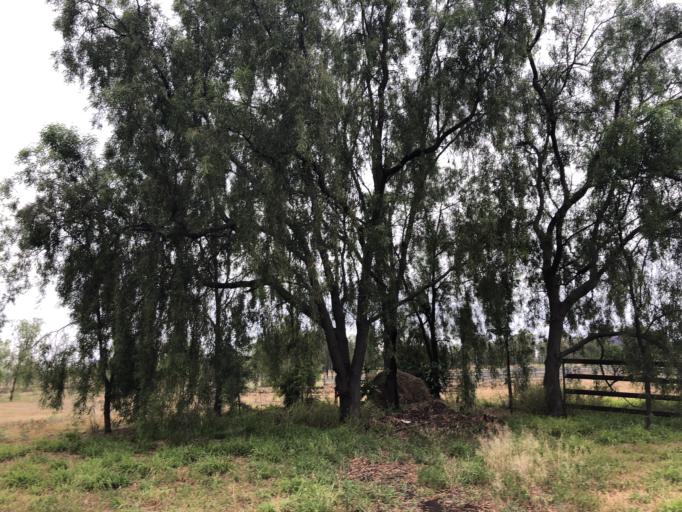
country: AU
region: Queensland
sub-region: Lockyer Valley
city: Gatton
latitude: -27.5868
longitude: 152.3440
